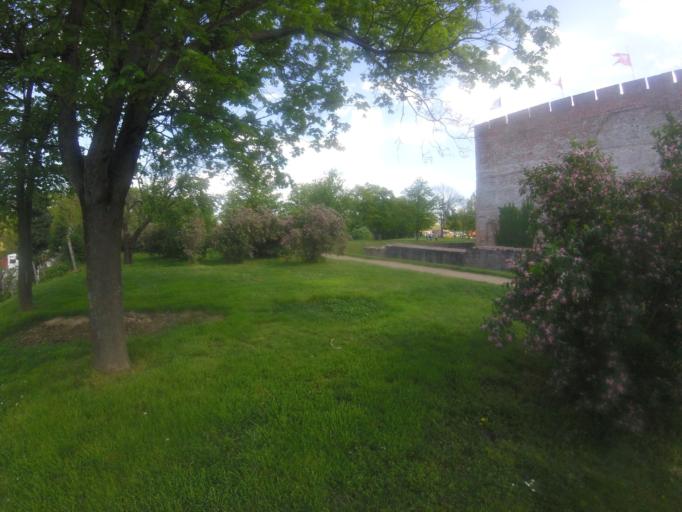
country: HU
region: Bekes
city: Gyula
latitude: 46.6464
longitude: 21.2857
